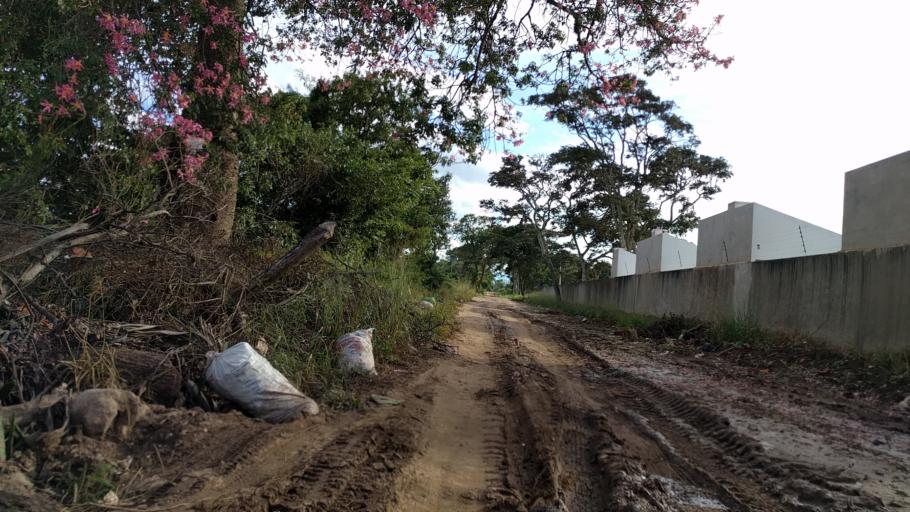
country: BO
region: Santa Cruz
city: Santa Cruz de la Sierra
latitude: -17.8515
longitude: -63.2590
